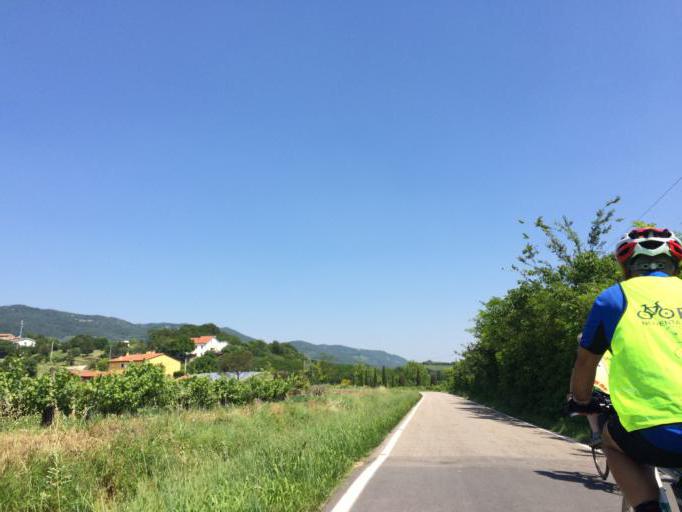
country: IT
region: Veneto
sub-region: Provincia di Vicenza
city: Barbarano Vicentino
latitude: 45.3989
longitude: 11.5542
